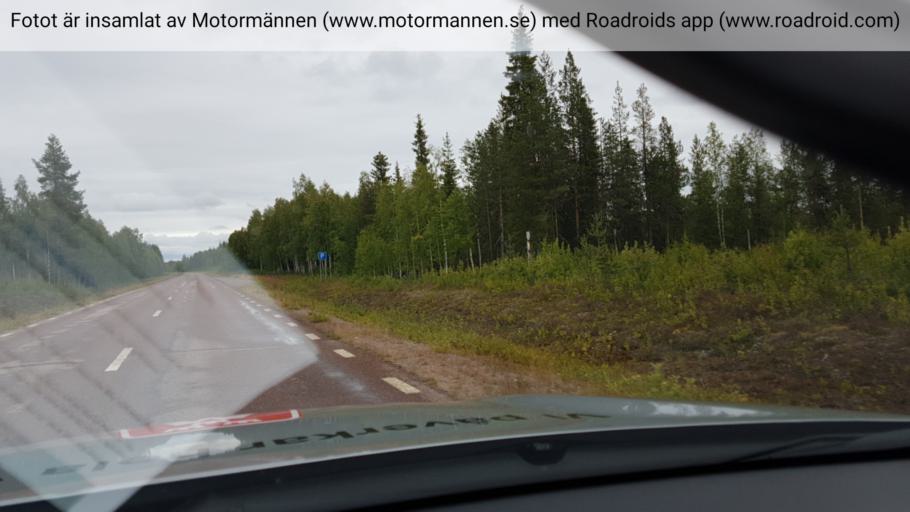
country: SE
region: Norrbotten
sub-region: Pajala Kommun
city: Pajala
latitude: 67.1425
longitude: 22.6173
